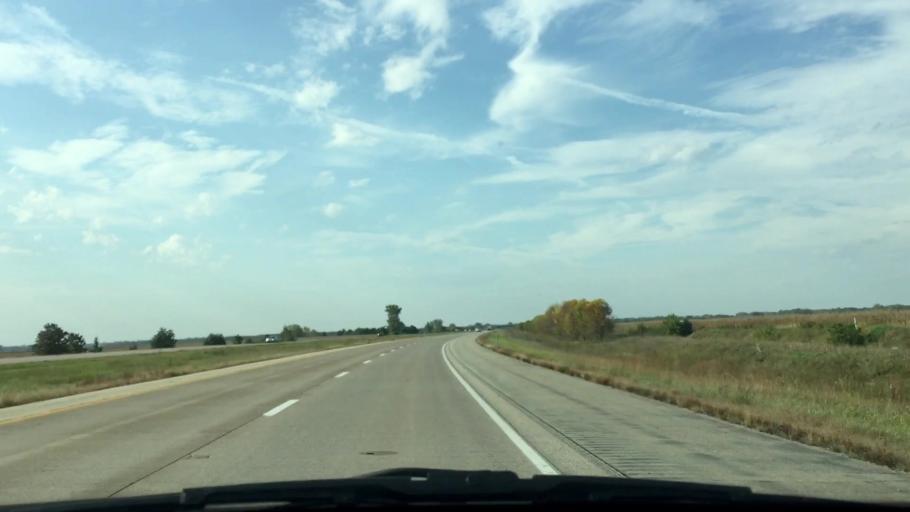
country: US
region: Illinois
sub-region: Whiteside County
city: Erie
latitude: 41.6609
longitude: -90.1456
